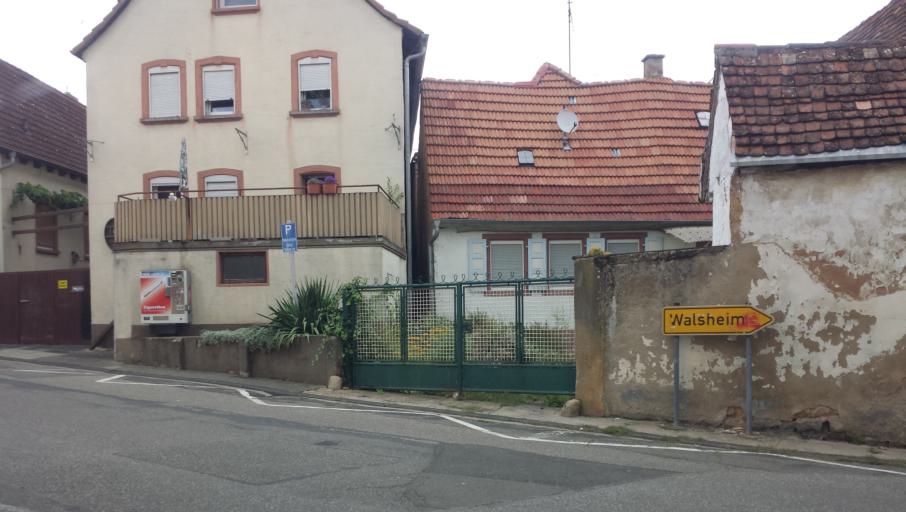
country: DE
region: Rheinland-Pfalz
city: Walsheim
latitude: 49.2254
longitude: 8.1118
